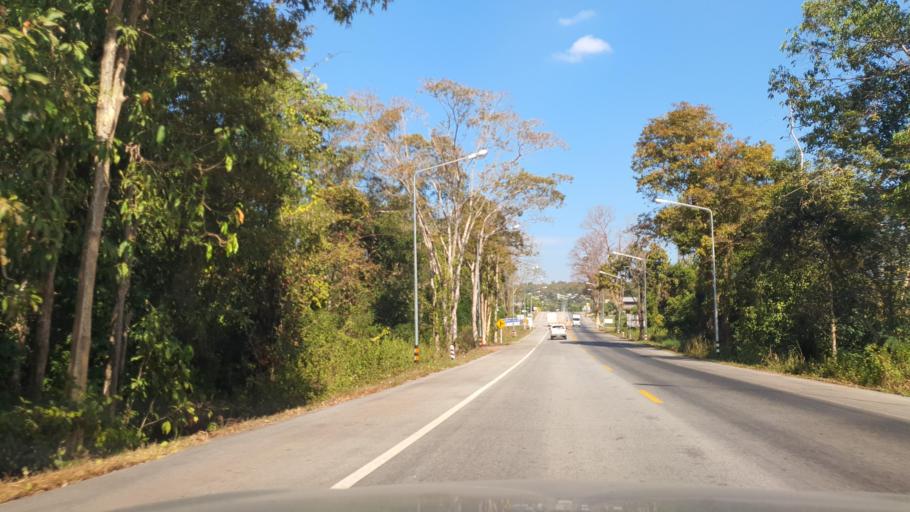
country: TH
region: Kalasin
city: Na Khu
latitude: 16.8545
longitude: 103.9305
